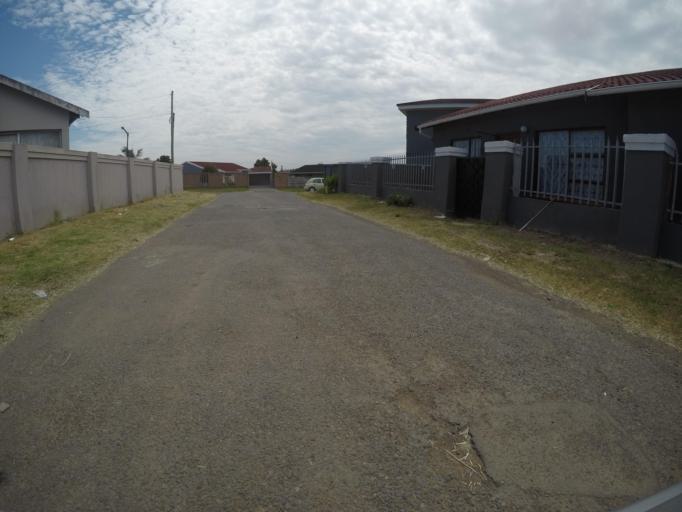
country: ZA
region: Eastern Cape
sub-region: Buffalo City Metropolitan Municipality
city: East London
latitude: -32.9914
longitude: 27.8678
